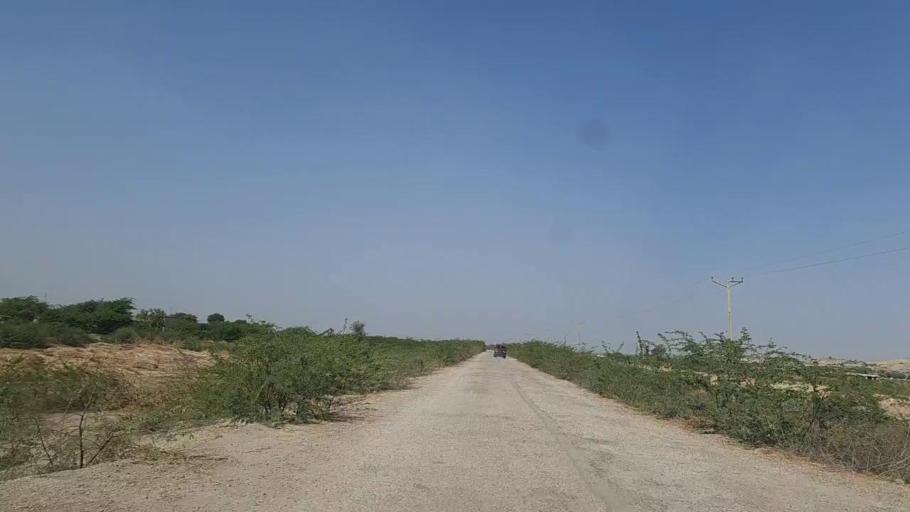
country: PK
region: Sindh
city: Naukot
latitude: 24.6328
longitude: 69.2883
